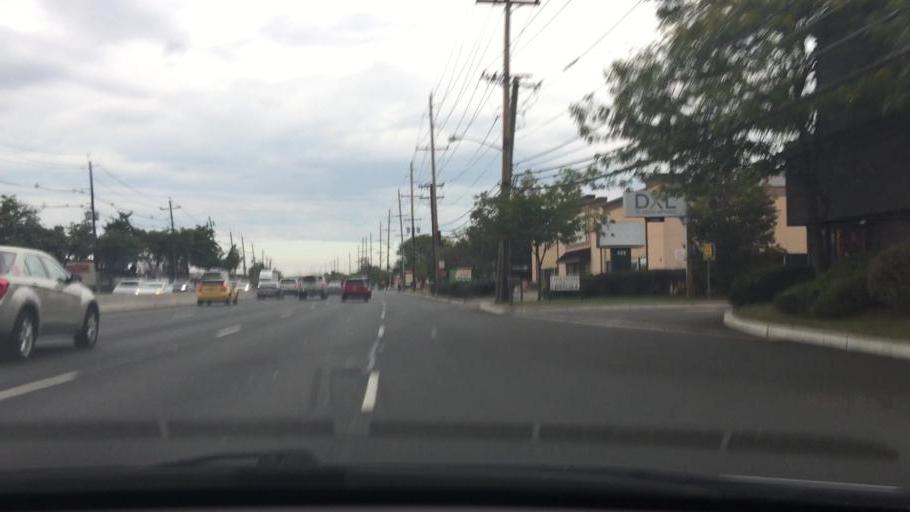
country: US
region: New Jersey
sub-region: Bergen County
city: Paramus
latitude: 40.9518
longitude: -74.0724
